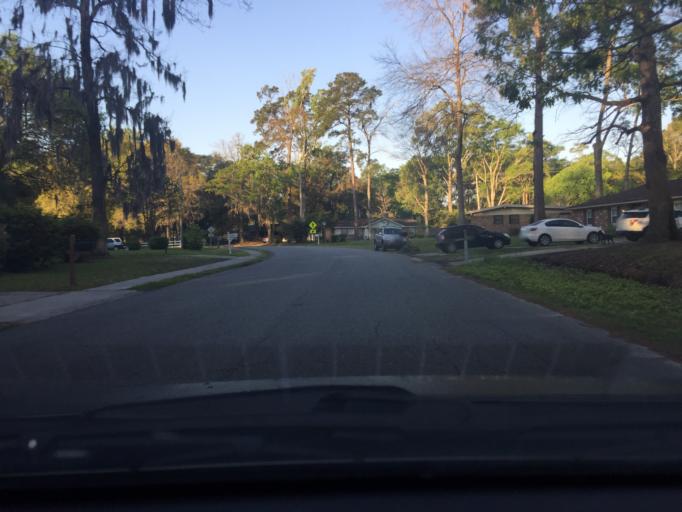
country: US
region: Georgia
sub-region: Chatham County
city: Montgomery
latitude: 31.9765
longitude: -81.1454
